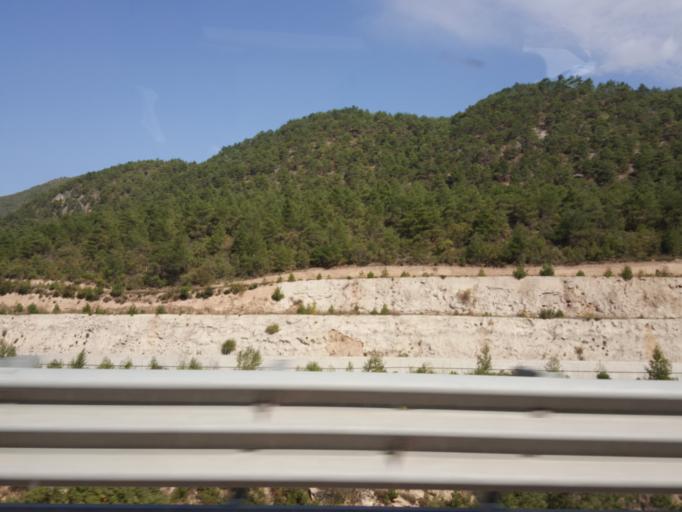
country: TR
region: Tokat
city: Basciftlik
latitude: 40.4529
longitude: 37.0585
